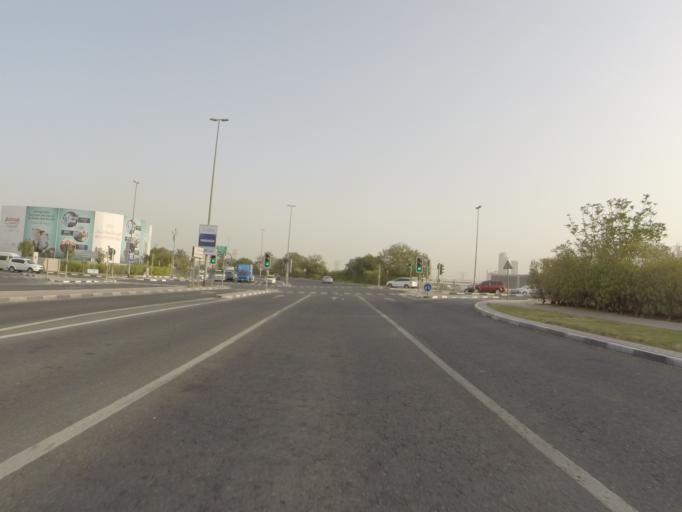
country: AE
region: Dubai
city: Dubai
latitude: 25.0506
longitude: 55.1267
